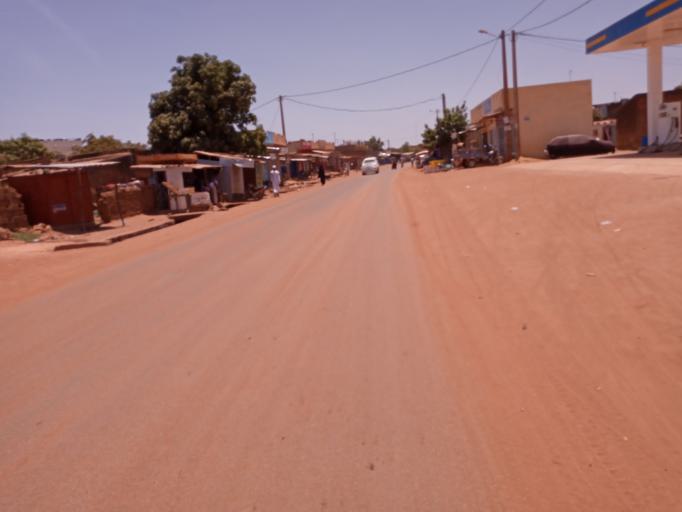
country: ML
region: Bamako
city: Bamako
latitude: 12.5775
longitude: -7.9710
